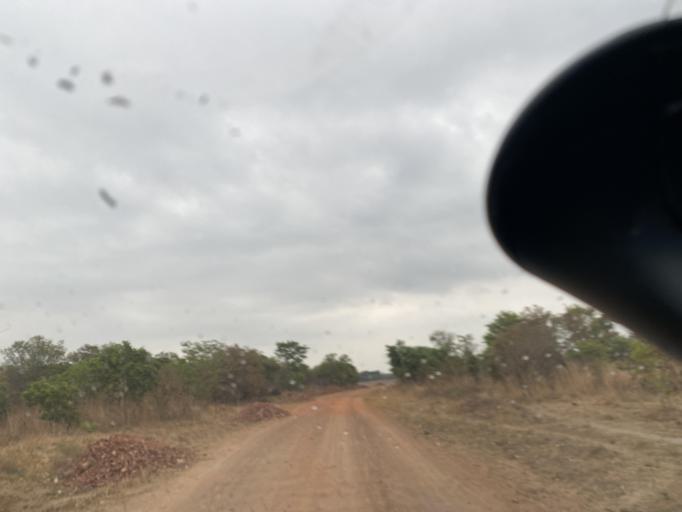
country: ZM
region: Lusaka
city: Chongwe
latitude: -15.1584
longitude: 28.7507
